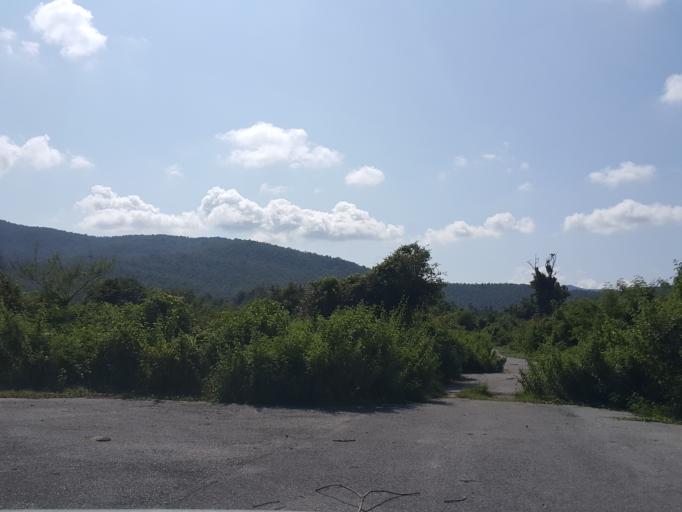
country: TH
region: Chiang Mai
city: Mae On
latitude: 18.8036
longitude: 99.1869
